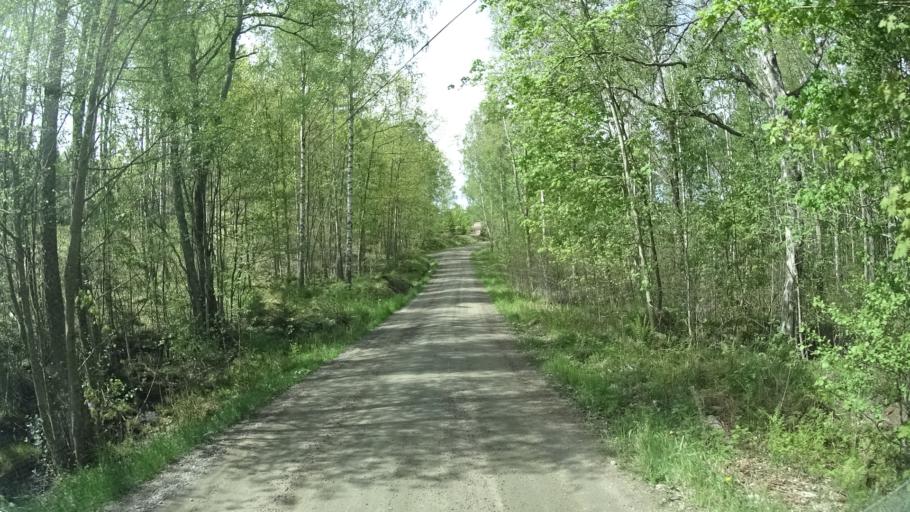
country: SE
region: OEstergoetland
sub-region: Finspangs Kommun
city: Finspang
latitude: 58.7546
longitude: 15.8342
